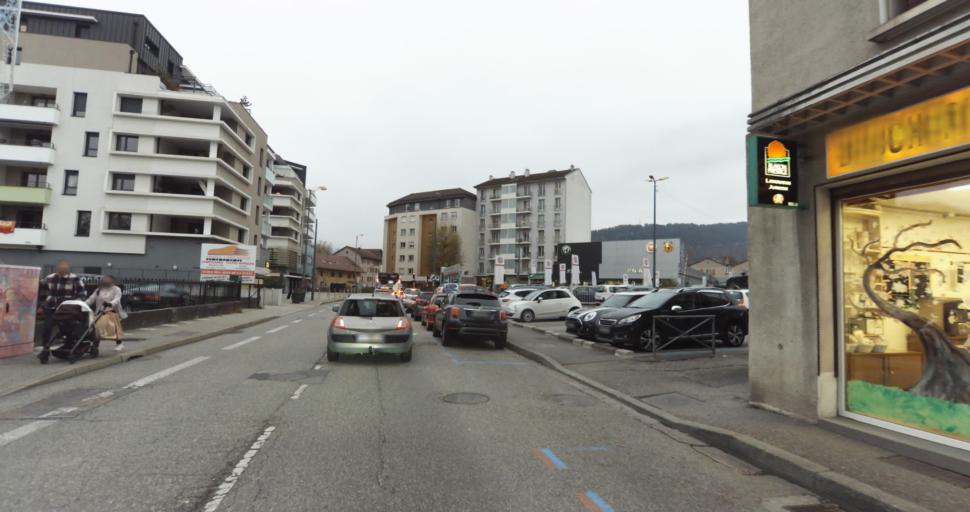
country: FR
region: Rhone-Alpes
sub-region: Departement de la Haute-Savoie
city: Annecy
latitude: 45.8980
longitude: 6.1131
